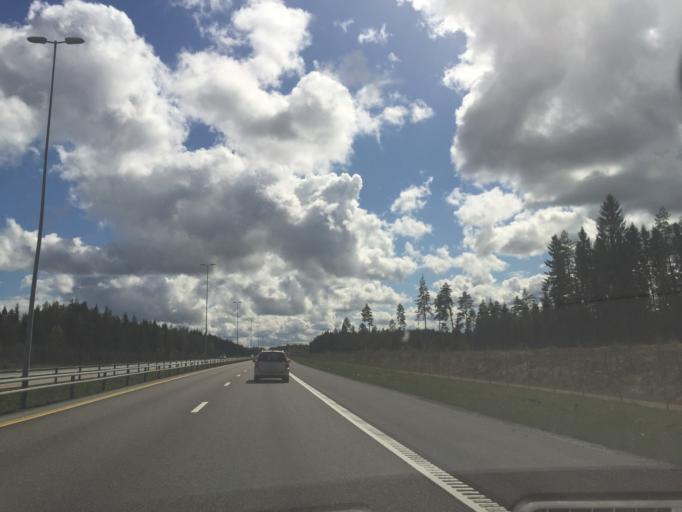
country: NO
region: Akershus
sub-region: Ullensaker
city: Jessheim
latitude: 60.2071
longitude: 11.1867
